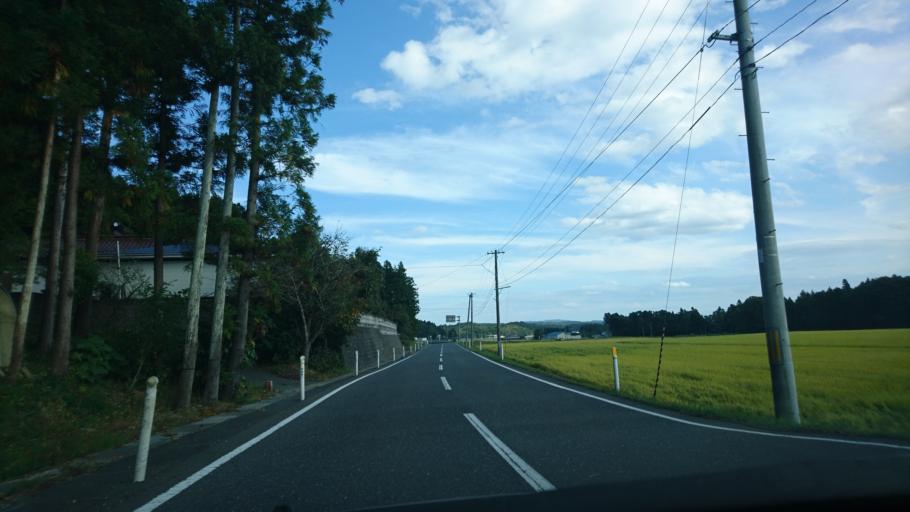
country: JP
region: Iwate
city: Ichinoseki
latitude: 38.8617
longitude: 141.1450
